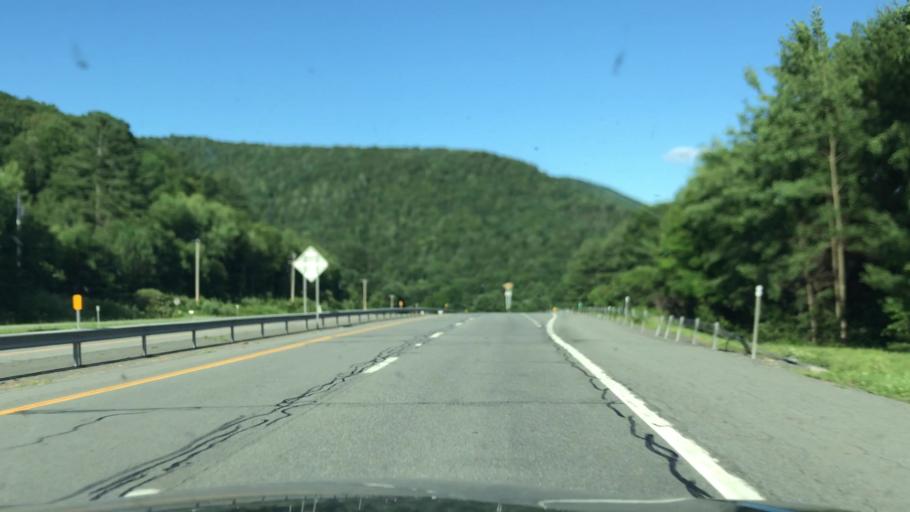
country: US
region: New York
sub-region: Delaware County
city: Hancock
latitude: 41.9929
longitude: -75.1381
